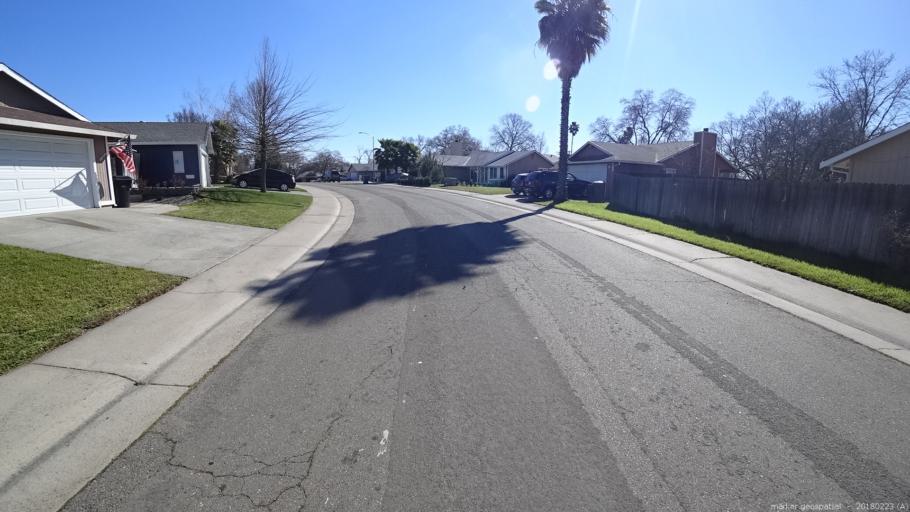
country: US
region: California
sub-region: Sacramento County
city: North Highlands
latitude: 38.7095
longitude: -121.3939
